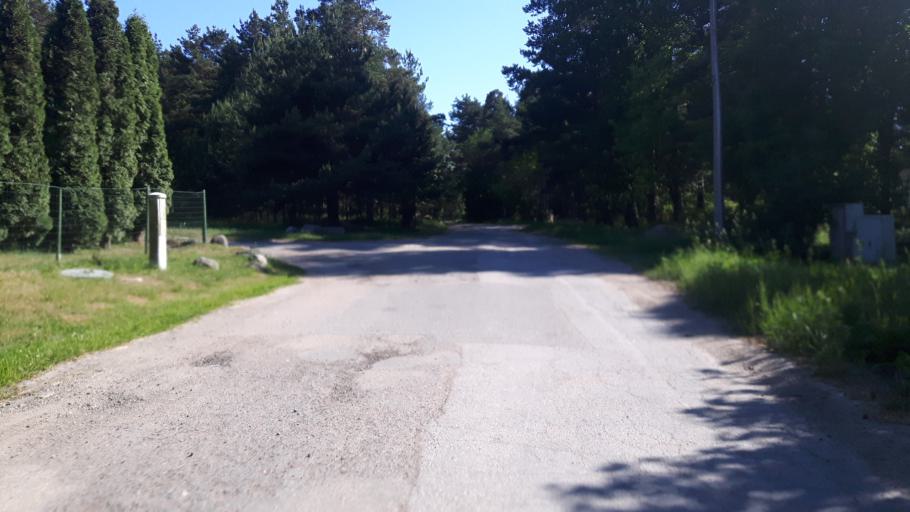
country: LV
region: Salacgrivas
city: Salacgriva
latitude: 57.7440
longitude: 24.3526
